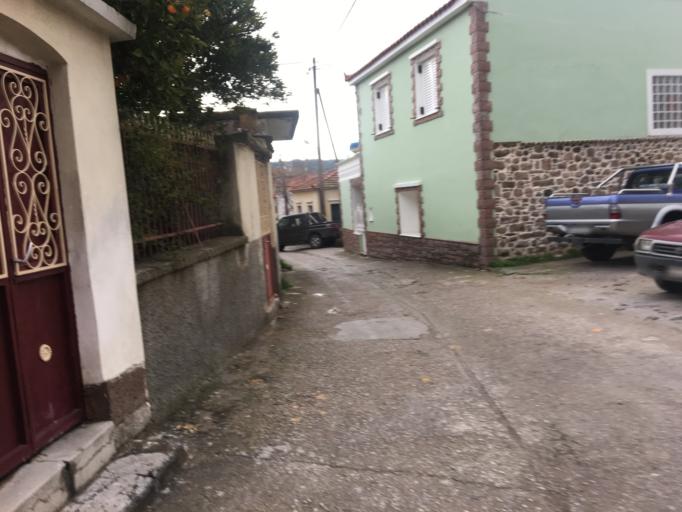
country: GR
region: North Aegean
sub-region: Nomos Lesvou
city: Agia Paraskevi
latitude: 39.2492
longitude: 26.2703
